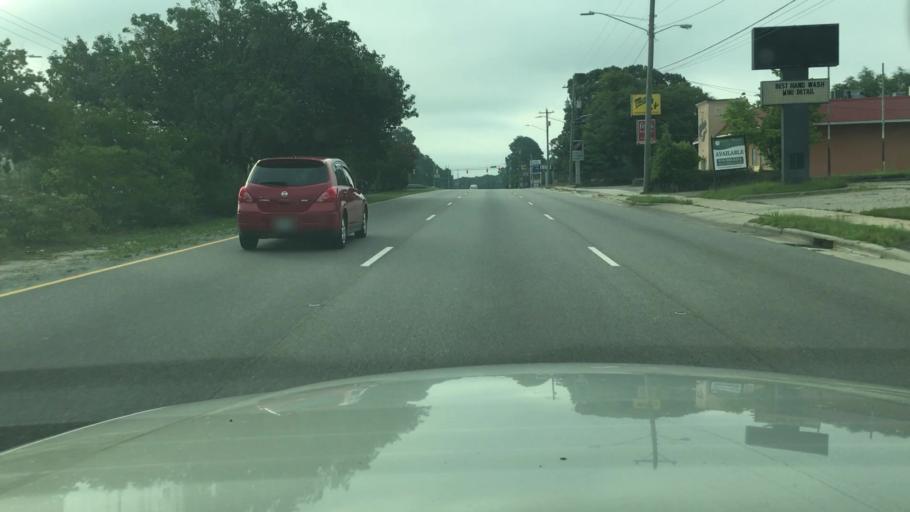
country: US
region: North Carolina
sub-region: Cumberland County
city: Fayetteville
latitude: 35.0730
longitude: -78.9253
